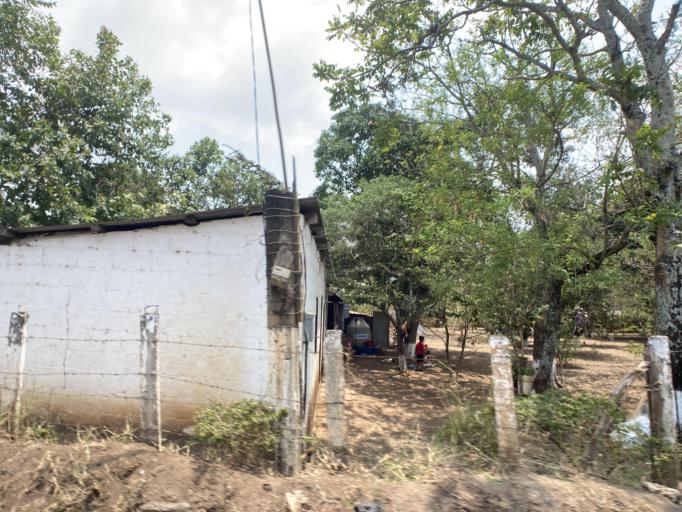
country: GT
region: Santa Rosa
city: Pueblo Nuevo Vinas
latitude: 14.3268
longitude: -90.5247
